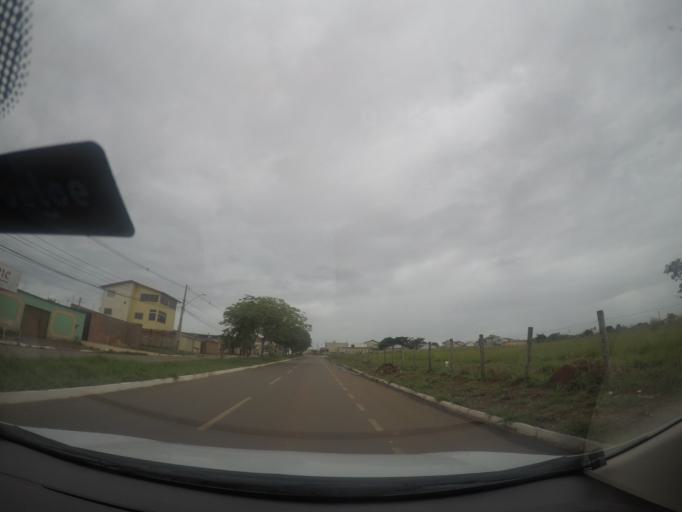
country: BR
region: Goias
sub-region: Goiania
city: Goiania
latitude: -16.6257
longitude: -49.3076
